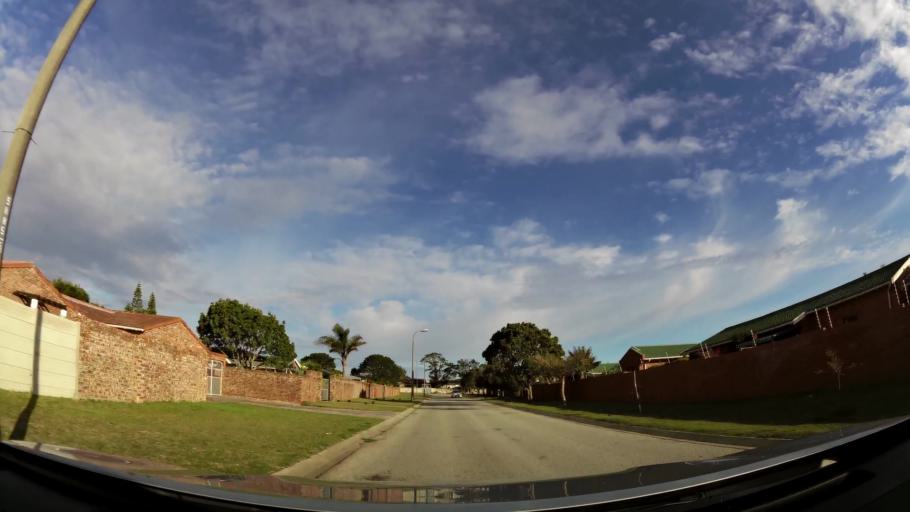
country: ZA
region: Eastern Cape
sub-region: Nelson Mandela Bay Metropolitan Municipality
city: Port Elizabeth
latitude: -33.9583
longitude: 25.4881
